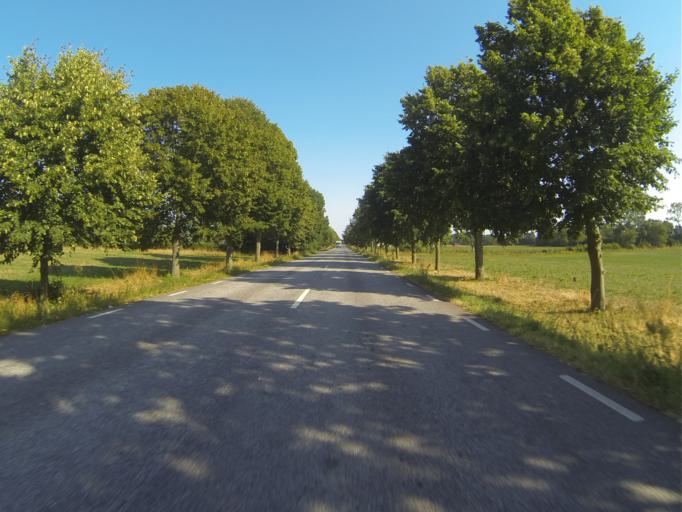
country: SE
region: Skane
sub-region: Hoors Kommun
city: Loberod
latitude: 55.7027
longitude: 13.5727
